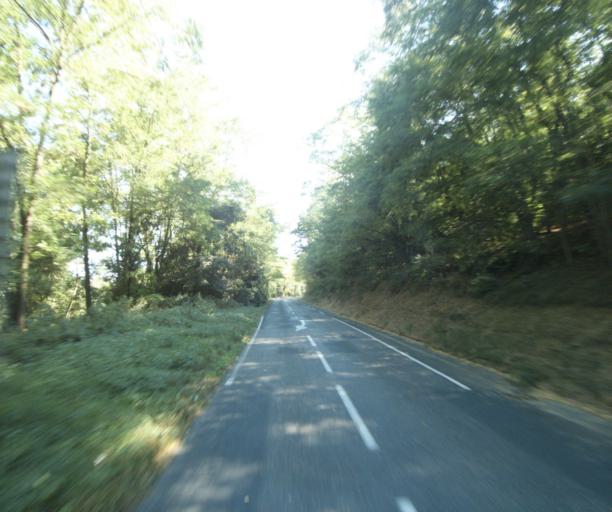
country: FR
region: Rhone-Alpes
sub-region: Departement du Rhone
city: Lissieu
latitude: 45.8431
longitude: 4.7241
